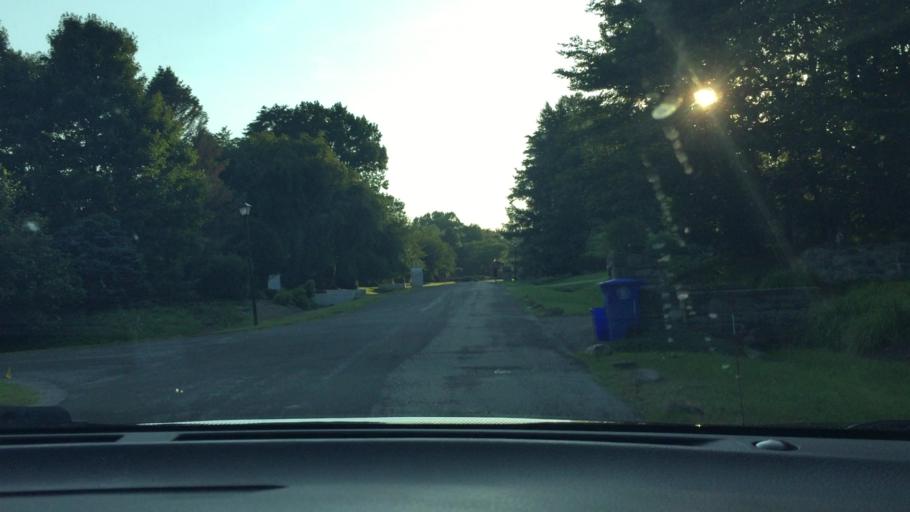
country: US
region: Maryland
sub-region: Montgomery County
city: Potomac
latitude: 39.0160
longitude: -77.1911
